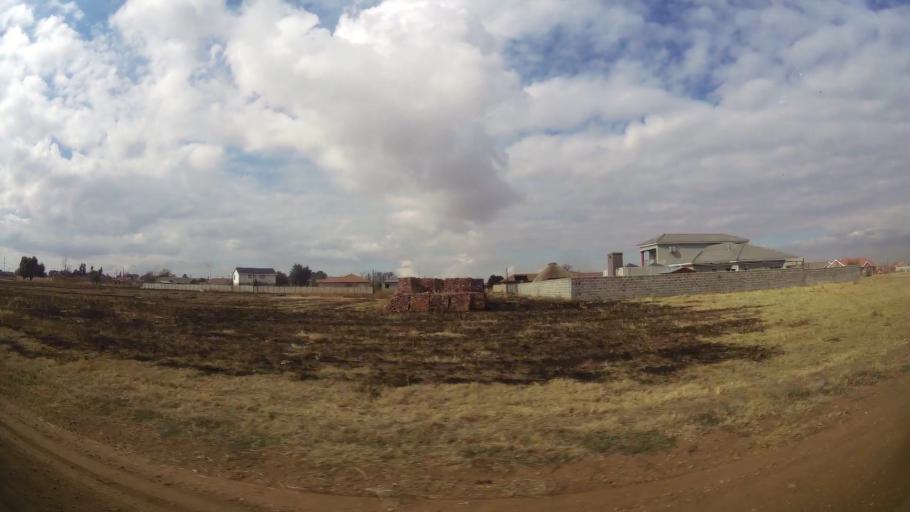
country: ZA
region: Gauteng
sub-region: Sedibeng District Municipality
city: Meyerton
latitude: -26.6071
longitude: 28.0503
